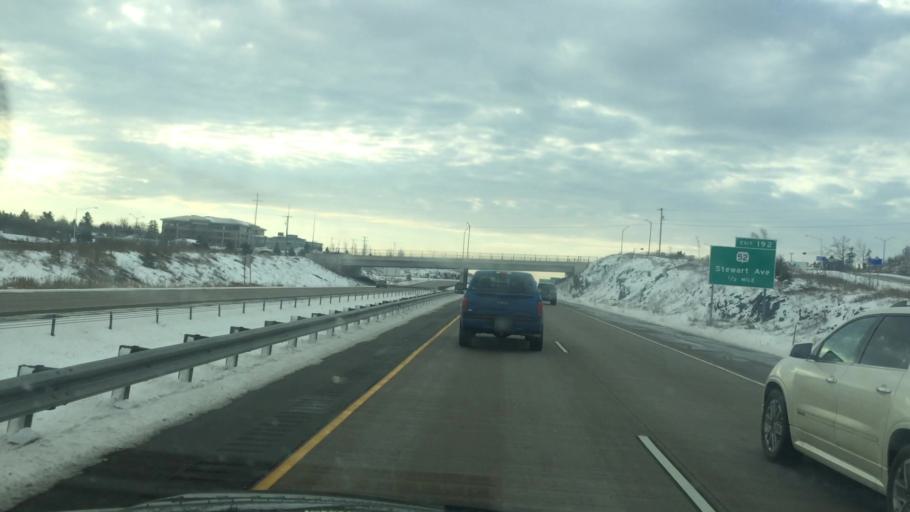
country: US
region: Wisconsin
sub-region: Marathon County
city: Wausau
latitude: 44.9718
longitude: -89.6567
